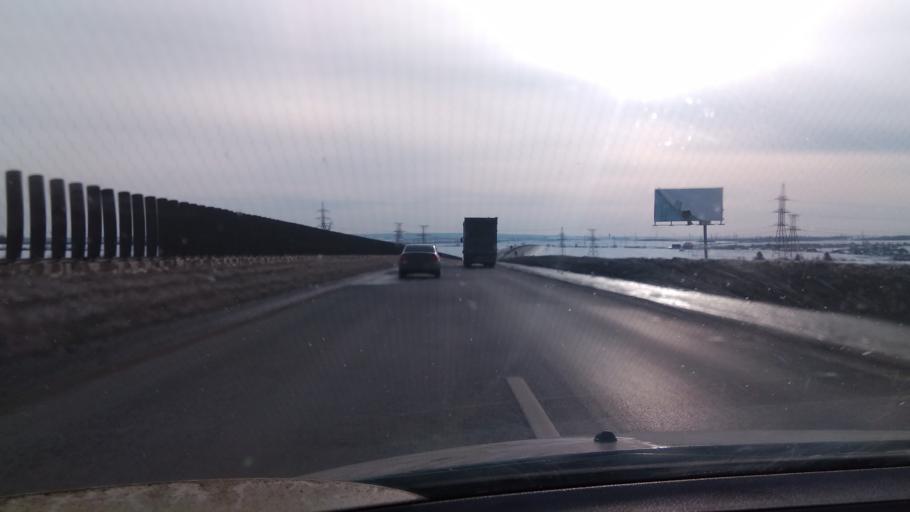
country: RU
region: Perm
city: Ferma
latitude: 57.9411
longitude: 56.3743
